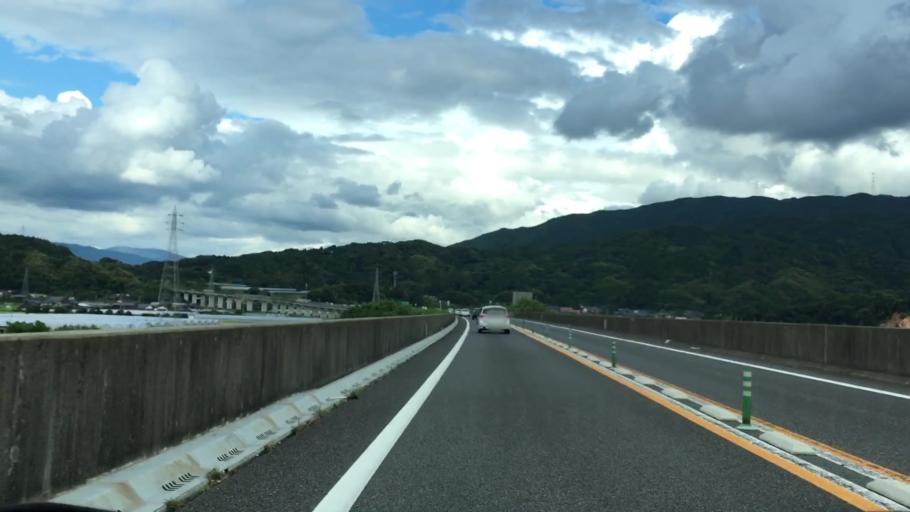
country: JP
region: Saga Prefecture
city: Karatsu
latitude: 33.4149
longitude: 130.0143
